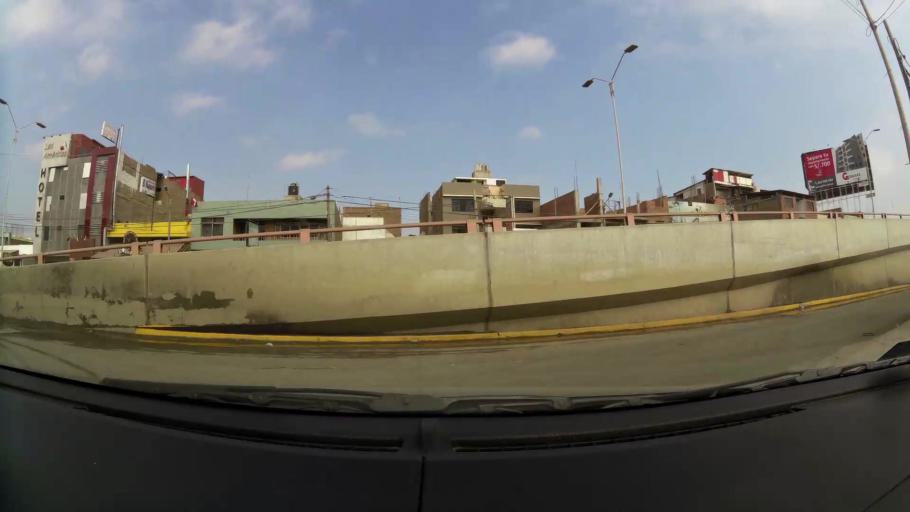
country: PE
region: La Libertad
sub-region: Provincia de Trujillo
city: Trujillo
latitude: -8.1222
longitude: -79.0219
